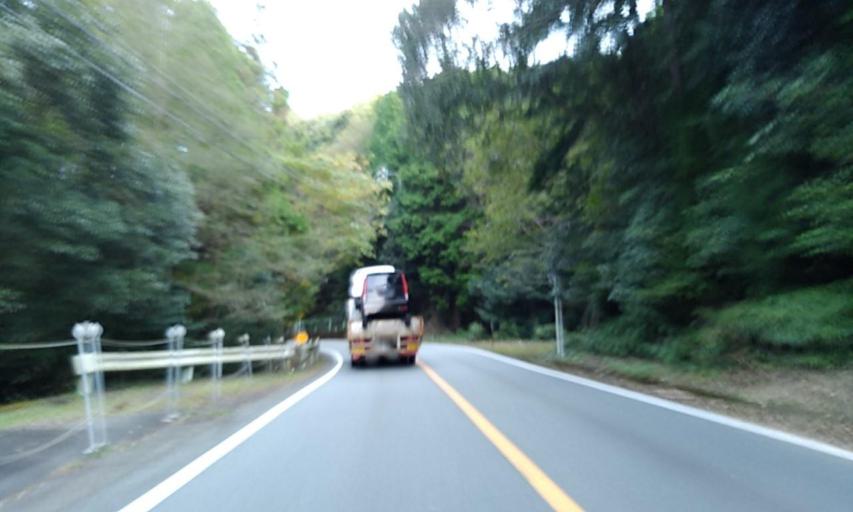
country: JP
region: Mie
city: Toba
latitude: 34.4036
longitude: 136.7795
